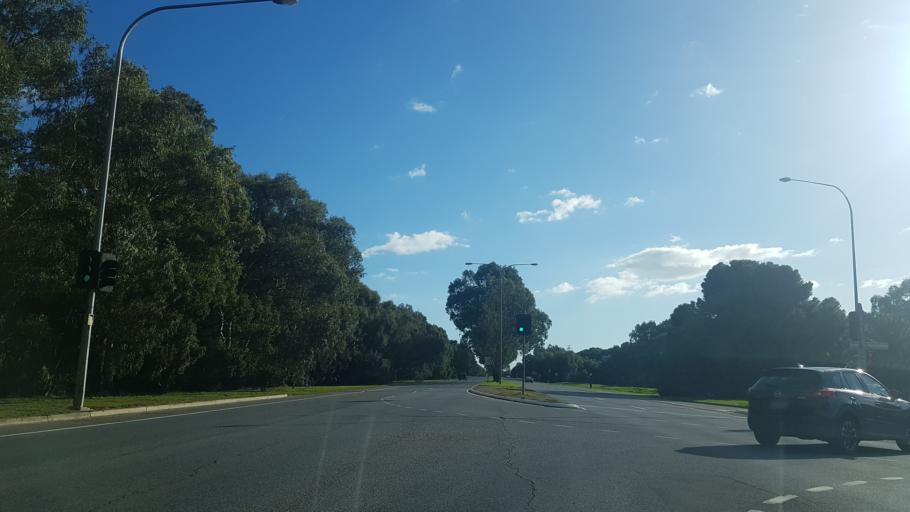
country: AU
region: South Australia
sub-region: Salisbury
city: Ingle Farm
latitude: -34.8250
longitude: 138.6143
